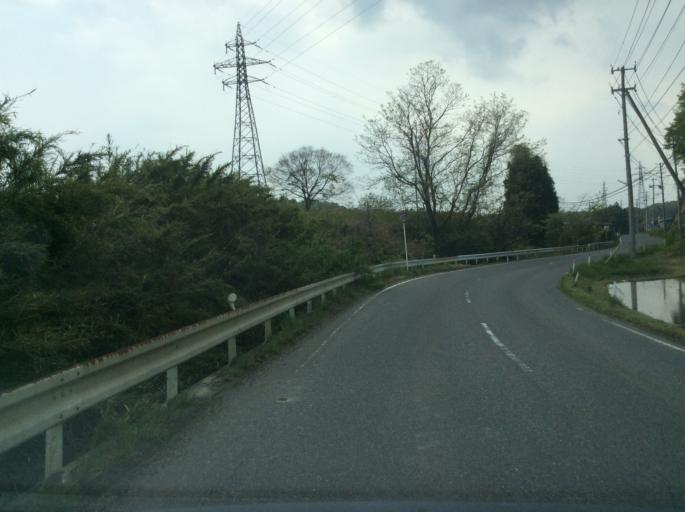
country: JP
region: Fukushima
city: Koriyama
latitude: 37.3879
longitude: 140.4274
